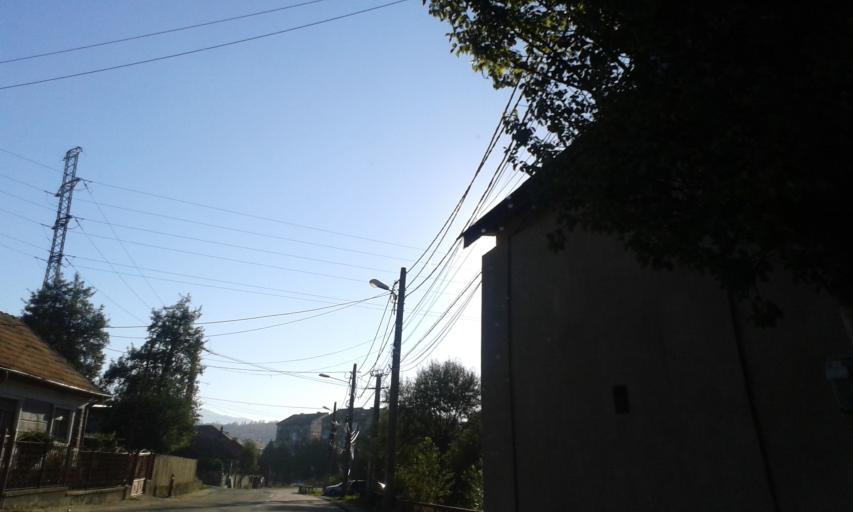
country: RO
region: Hunedoara
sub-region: Municipiul Petrosani
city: Petrosani
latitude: 45.4240
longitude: 23.3778
